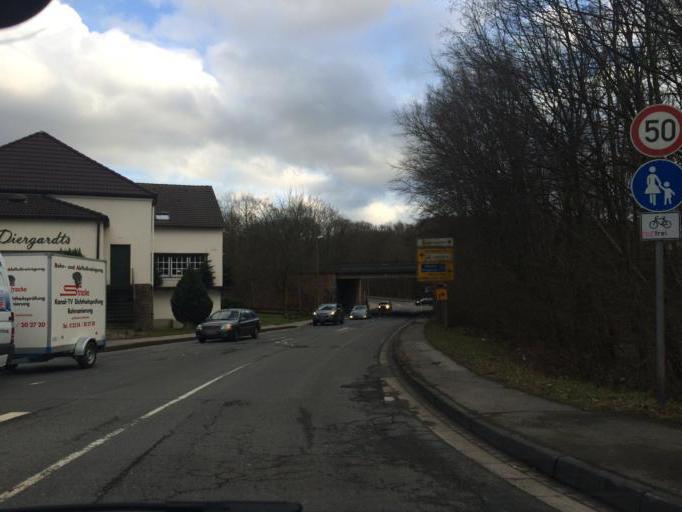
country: DE
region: North Rhine-Westphalia
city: Hattingen
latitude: 51.4051
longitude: 7.2037
